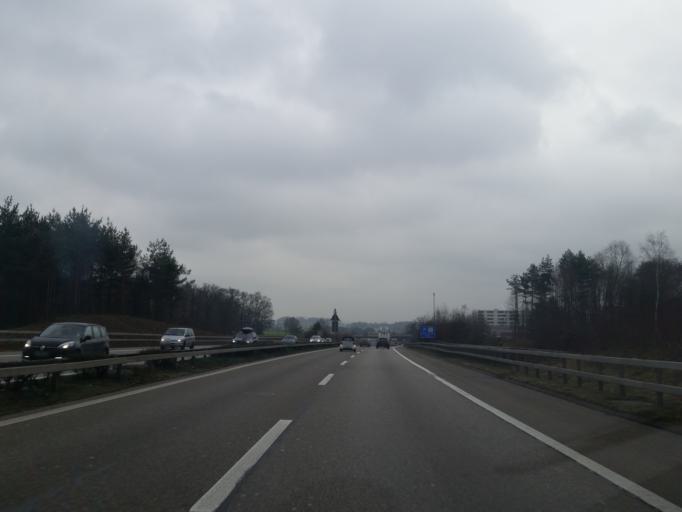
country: CH
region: Zurich
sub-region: Bezirk Zuerich
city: Zuerich (Kreis 10) / Ruetihof
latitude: 47.4260
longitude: 8.4905
